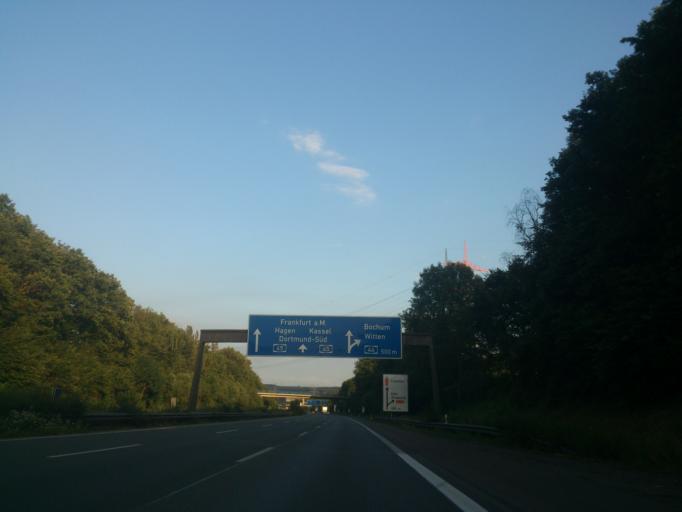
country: DE
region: North Rhine-Westphalia
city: Witten
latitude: 51.4714
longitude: 7.3994
